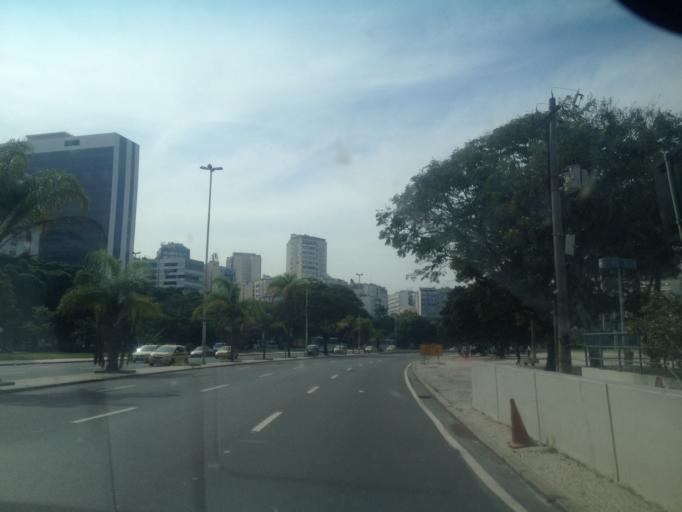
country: BR
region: Rio de Janeiro
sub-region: Rio De Janeiro
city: Rio de Janeiro
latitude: -22.9436
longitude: -43.1806
